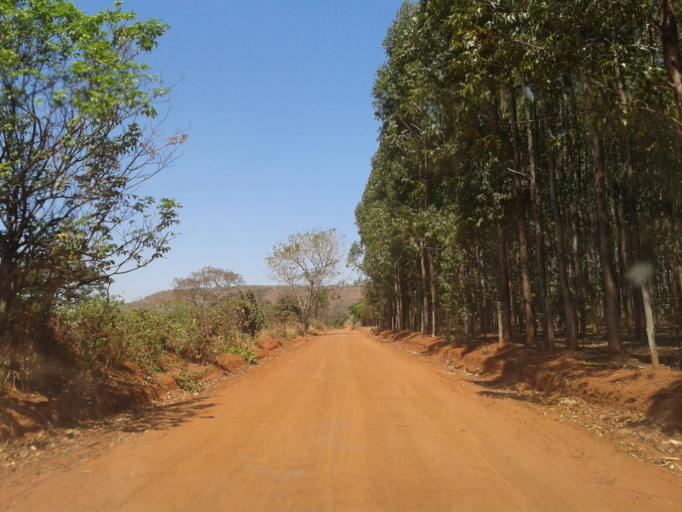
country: BR
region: Minas Gerais
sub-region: Ituiutaba
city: Ituiutaba
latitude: -19.0780
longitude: -49.3143
